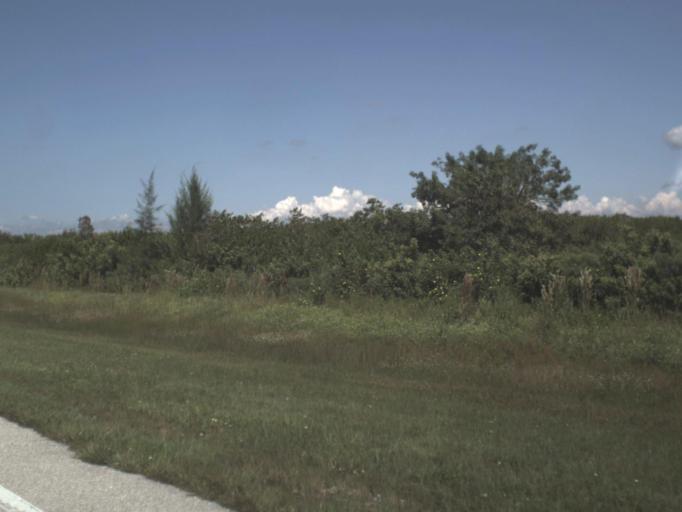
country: US
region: Florida
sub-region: Lee County
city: Pine Island Center
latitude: 26.6149
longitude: -82.0386
